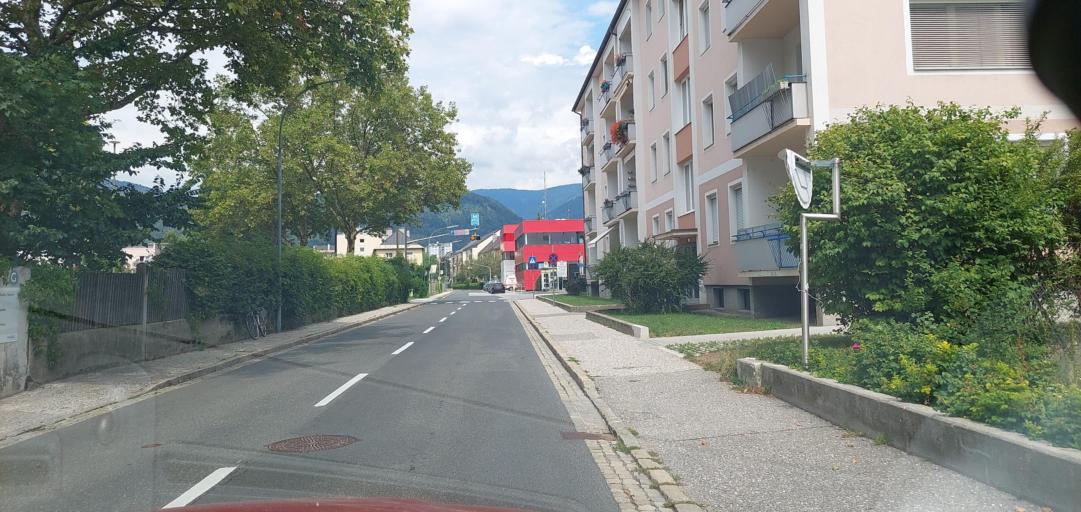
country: AT
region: Carinthia
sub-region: Villach Stadt
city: Villach
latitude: 46.6155
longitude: 13.8553
